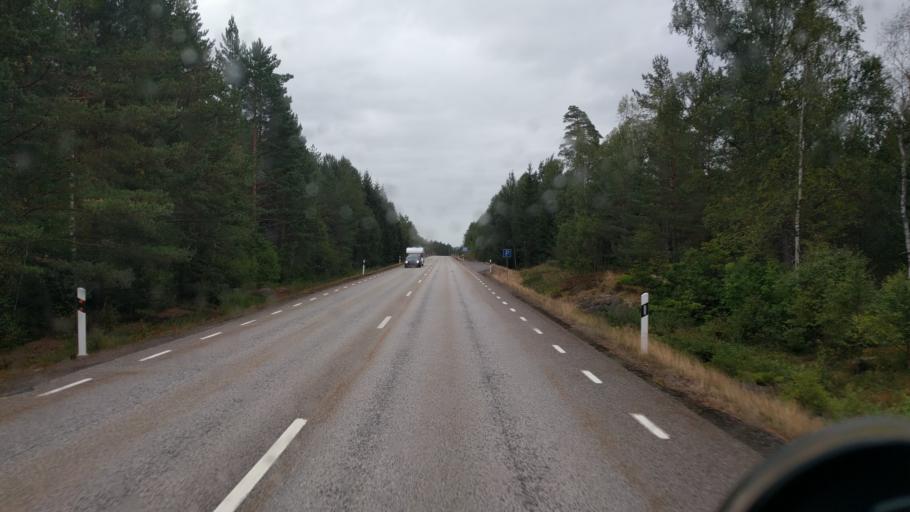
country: SE
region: Kalmar
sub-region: Vasterviks Kommun
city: Ankarsrum
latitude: 57.6995
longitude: 16.2601
